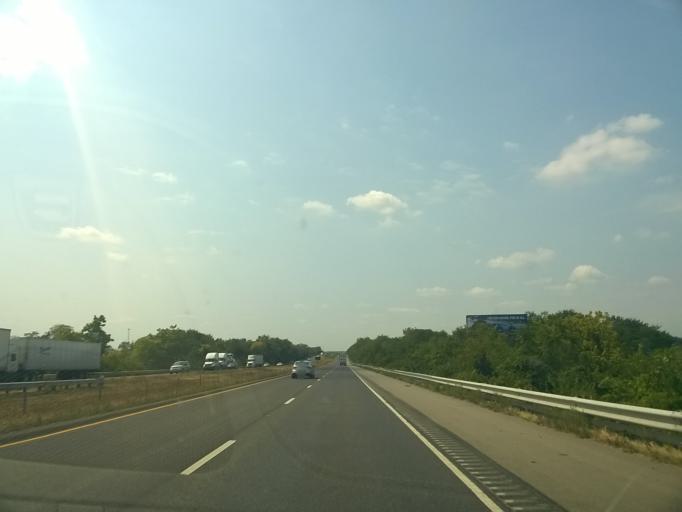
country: US
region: Indiana
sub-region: Vigo County
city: Terre Haute
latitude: 39.4314
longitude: -87.3975
